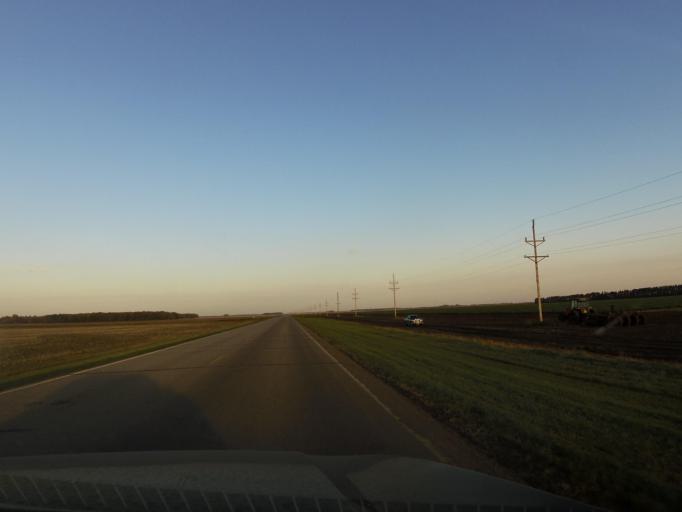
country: CA
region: Manitoba
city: Altona
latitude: 48.9631
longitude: -97.6546
